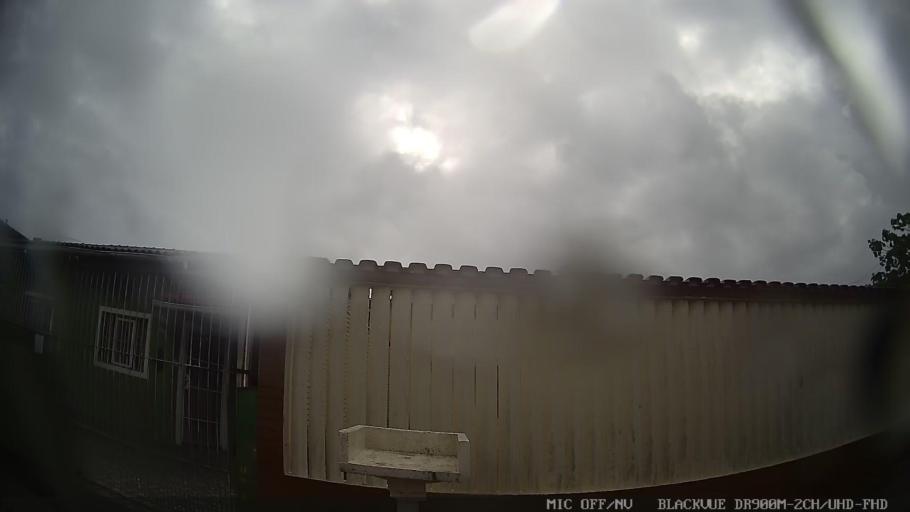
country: BR
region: Sao Paulo
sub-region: Itanhaem
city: Itanhaem
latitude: -24.1953
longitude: -46.8110
